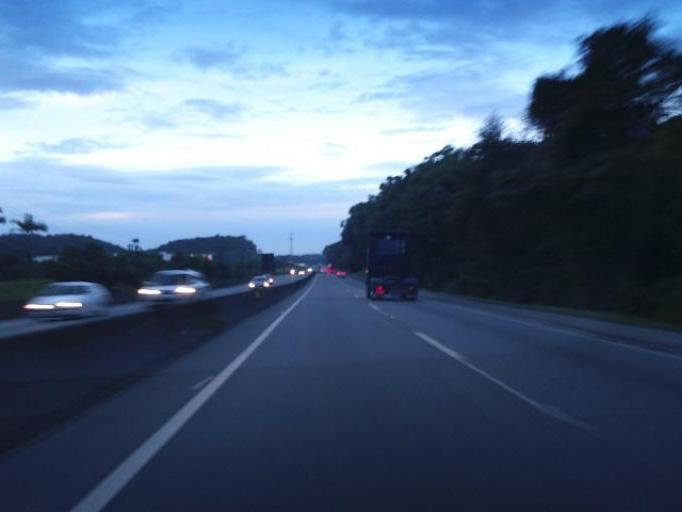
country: BR
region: Santa Catarina
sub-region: Joinville
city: Joinville
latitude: -26.2358
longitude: -48.9153
